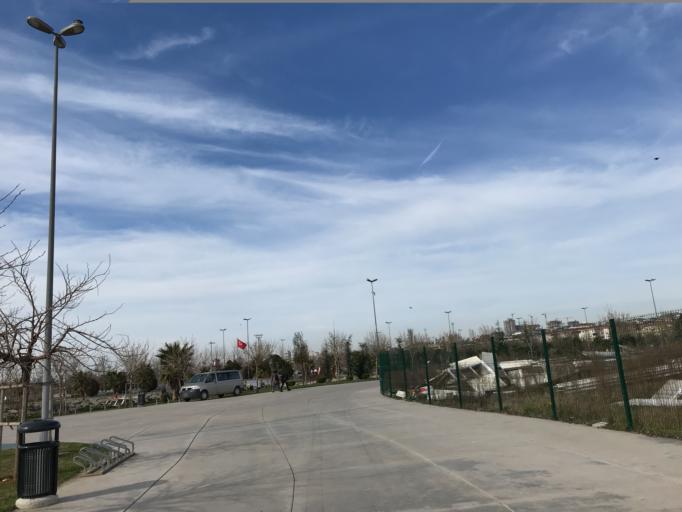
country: TR
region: Istanbul
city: Maltepe
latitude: 40.9317
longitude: 29.1148
